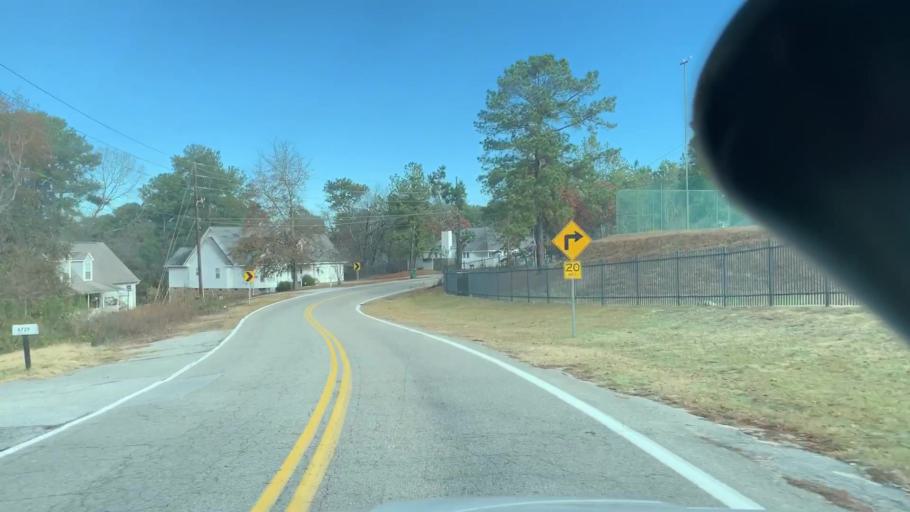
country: US
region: South Carolina
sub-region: Richland County
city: Woodfield
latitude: 34.0663
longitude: -80.9311
